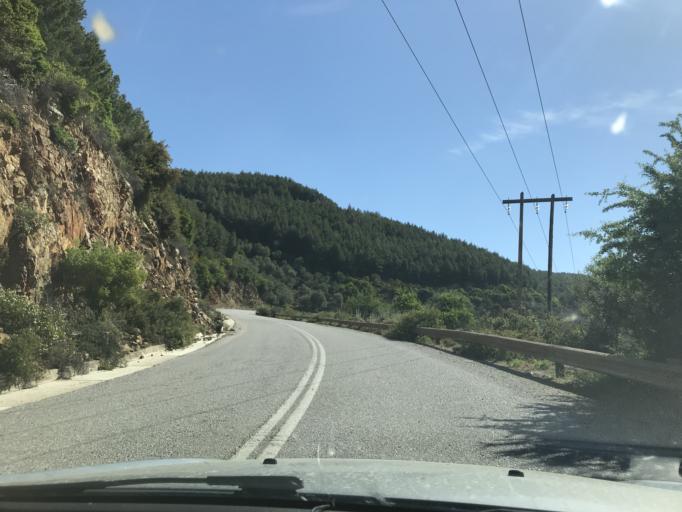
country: GR
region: Central Macedonia
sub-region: Nomos Chalkidikis
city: Sykia
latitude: 39.9622
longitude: 23.9327
